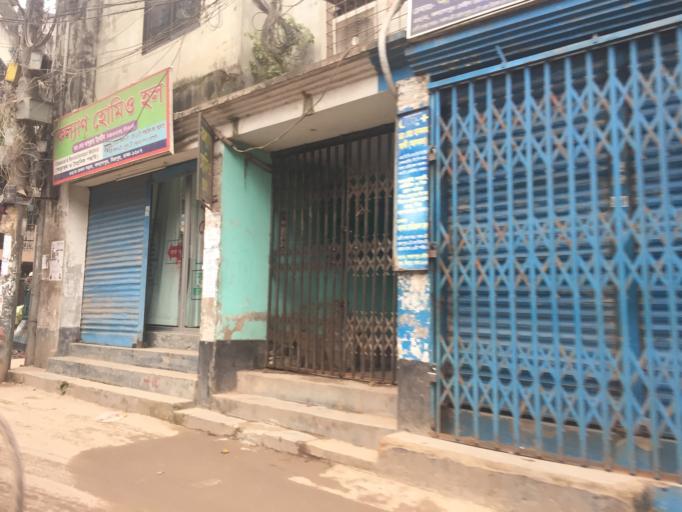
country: BD
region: Dhaka
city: Azimpur
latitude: 23.7821
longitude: 90.3599
